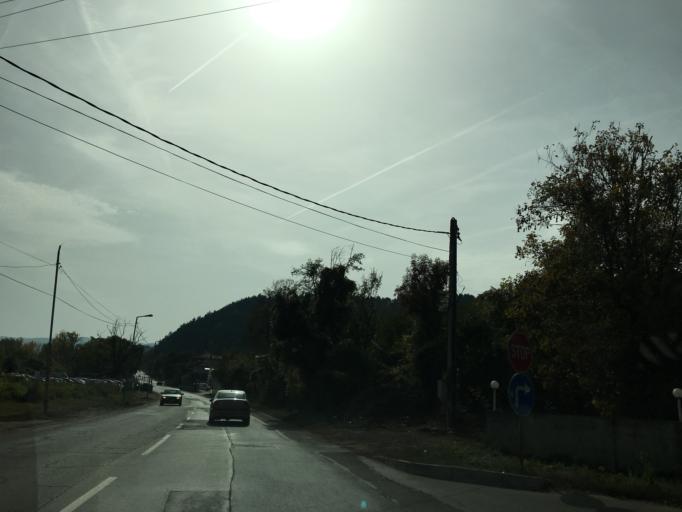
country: BG
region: Sofia-Capital
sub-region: Stolichna Obshtina
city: Sofia
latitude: 42.6098
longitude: 23.3995
